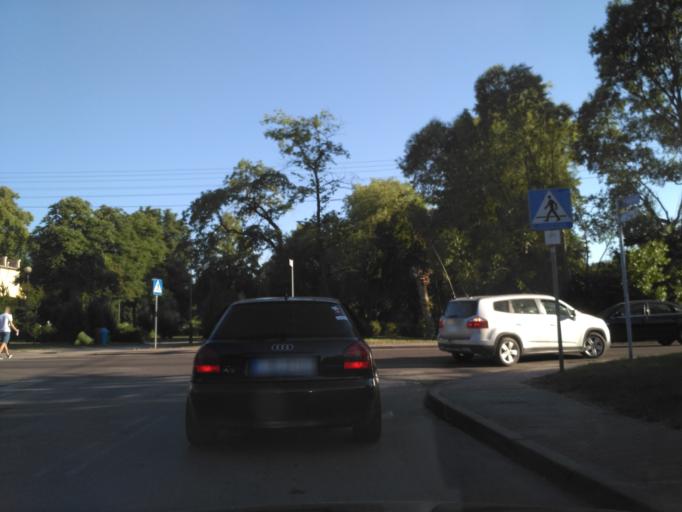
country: PL
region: Lublin Voivodeship
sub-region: Powiat lubelski
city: Bychawa
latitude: 51.0171
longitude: 22.5297
